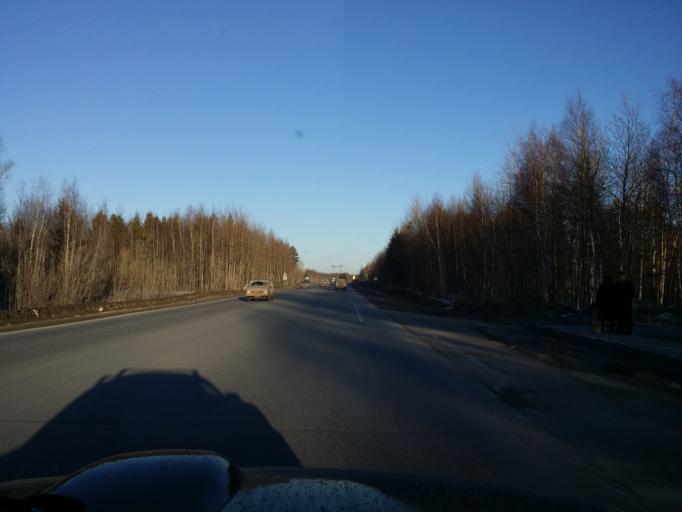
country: RU
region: Khanty-Mansiyskiy Avtonomnyy Okrug
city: Megion
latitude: 61.0518
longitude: 76.3253
